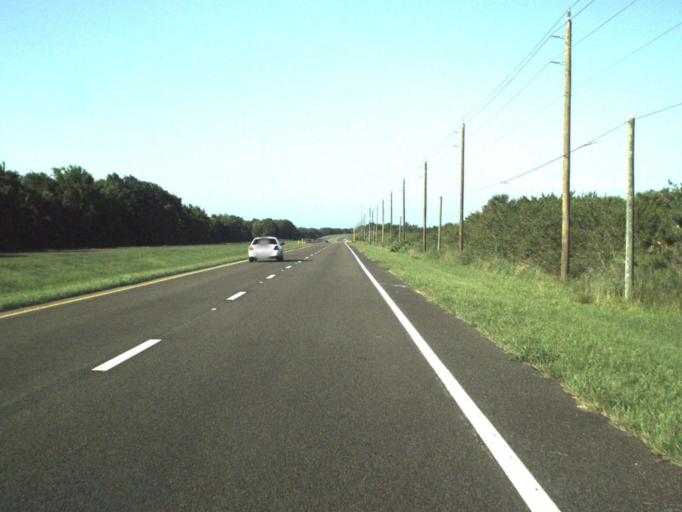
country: US
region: Florida
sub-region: Volusia County
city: Oak Hill
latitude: 28.8177
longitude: -80.8626
